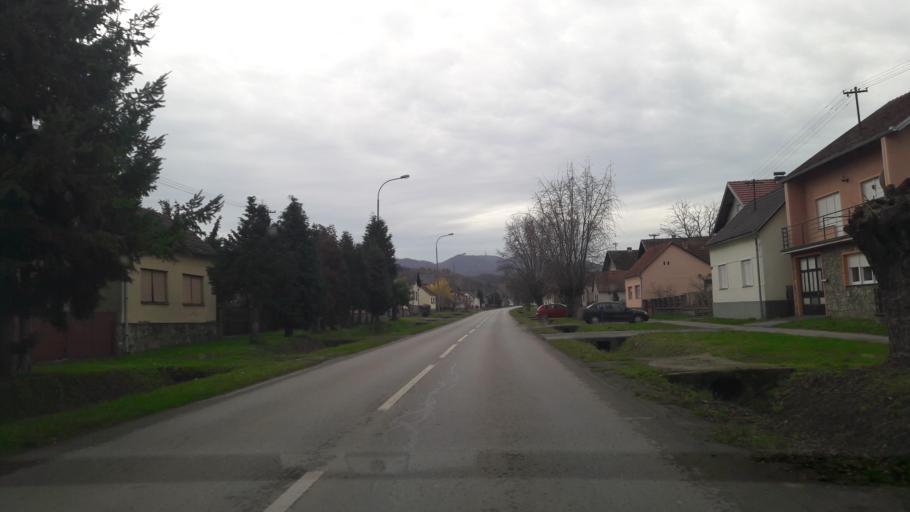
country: HR
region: Virovitick-Podravska
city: Orahovica
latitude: 45.5443
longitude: 17.8996
